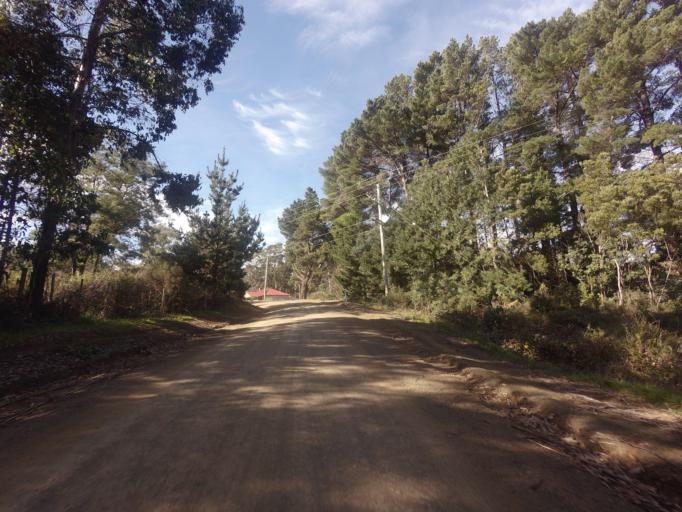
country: AU
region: Tasmania
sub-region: Clarence
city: Sandford
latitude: -43.1442
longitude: 147.7644
